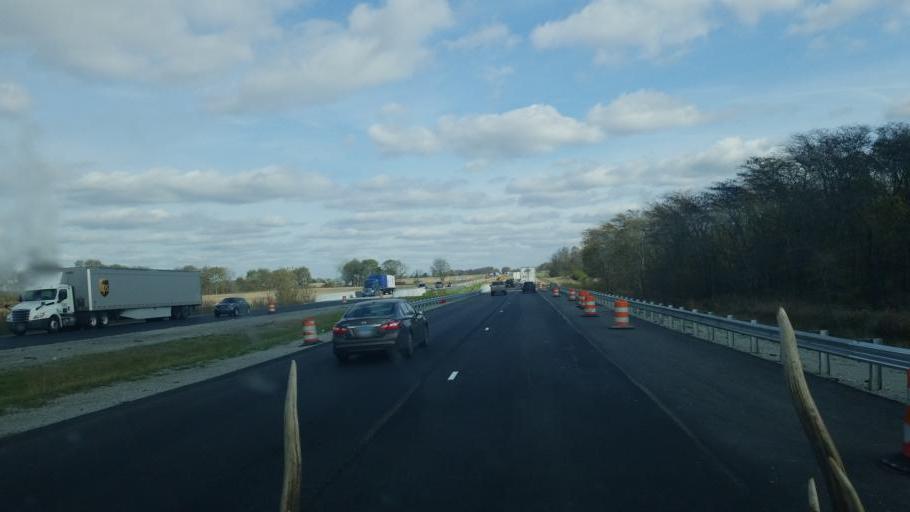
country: US
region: Indiana
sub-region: Henry County
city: Knightstown
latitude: 39.8275
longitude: -85.6026
